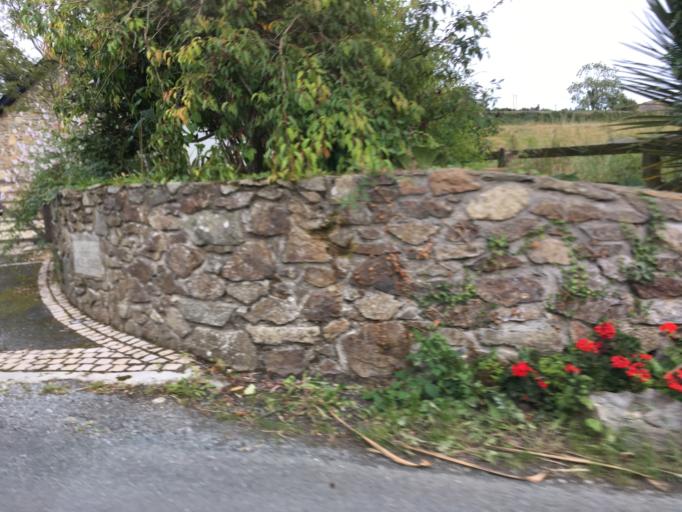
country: IE
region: Leinster
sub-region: Wicklow
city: Wicklow
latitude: 52.9142
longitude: -6.0801
